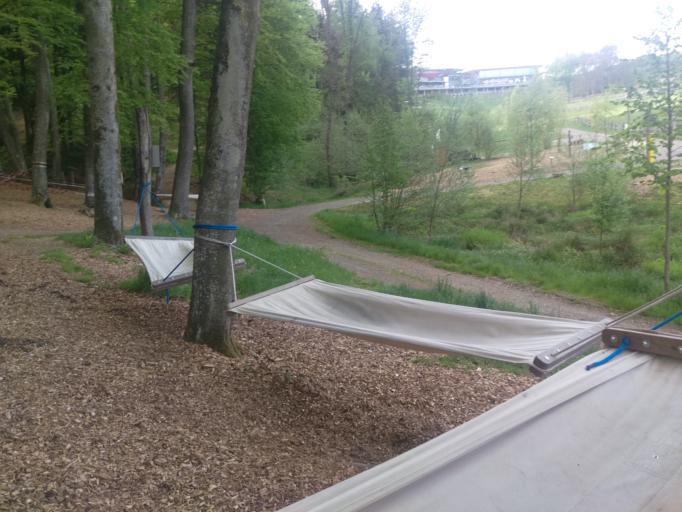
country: AT
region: Styria
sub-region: Politischer Bezirk Suedoststeiermark
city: Riegersburg
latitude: 46.9893
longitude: 15.9110
